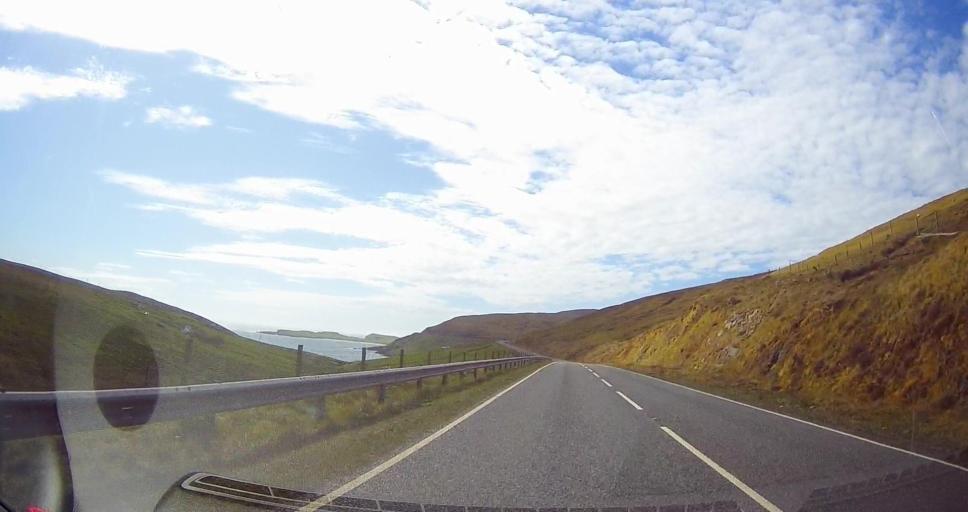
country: GB
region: Scotland
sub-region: Shetland Islands
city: Sandwick
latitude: 60.0002
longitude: -1.2795
